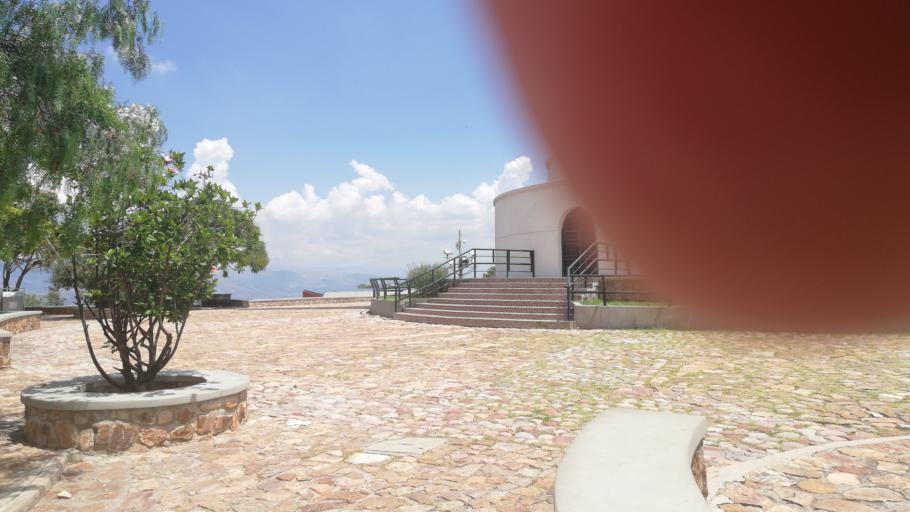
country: BO
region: Cochabamba
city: Cochabamba
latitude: -17.3843
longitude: -66.1347
